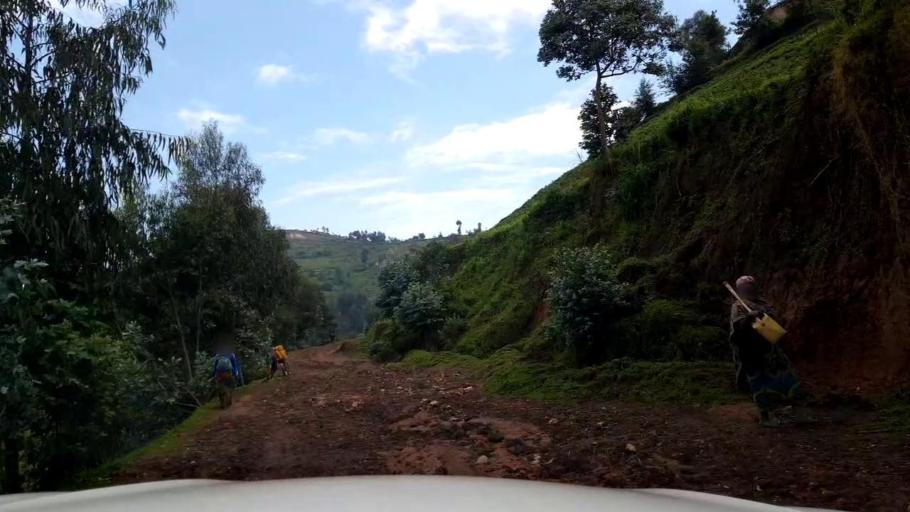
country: RW
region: Western Province
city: Gisenyi
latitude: -1.7177
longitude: 29.3901
